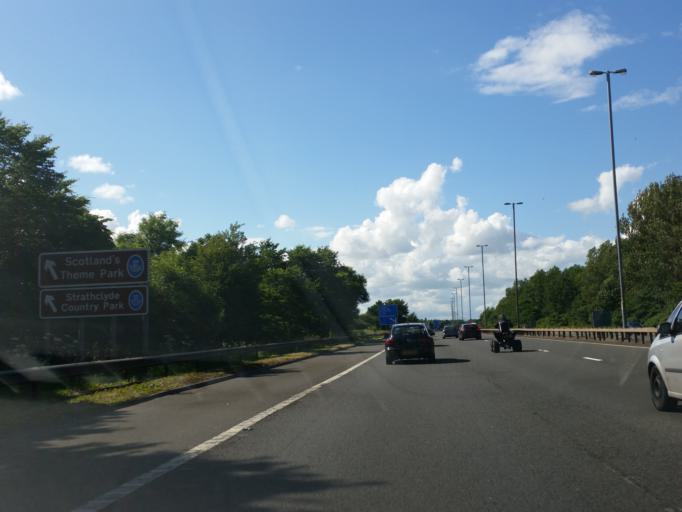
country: GB
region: Scotland
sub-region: South Lanarkshire
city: Hamilton
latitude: 55.7929
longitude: -4.0415
